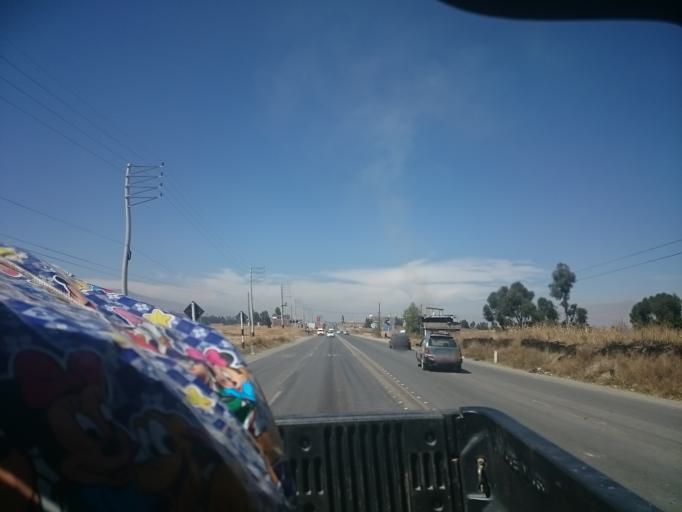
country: PE
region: Junin
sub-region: Provincia de Huancayo
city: San Agustin
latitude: -11.9787
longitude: -75.2644
